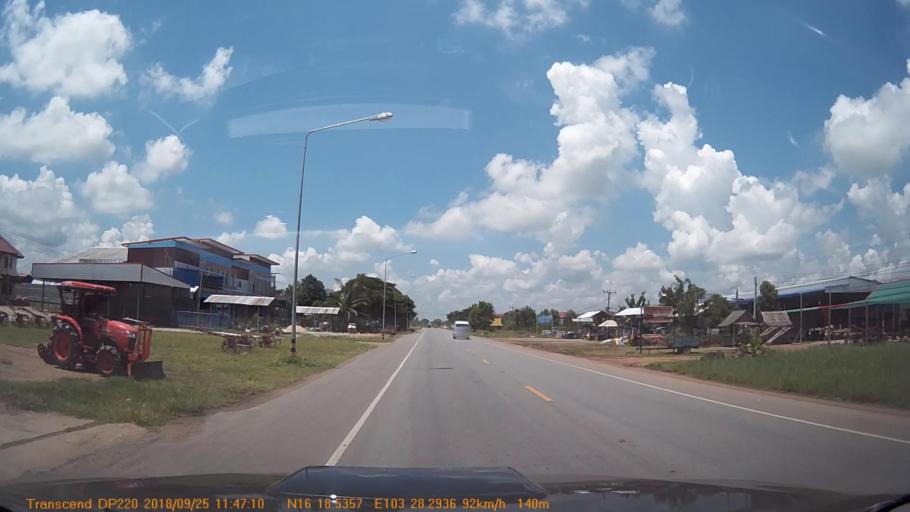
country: TH
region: Kalasin
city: Khong Chai
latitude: 16.3088
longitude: 103.4717
